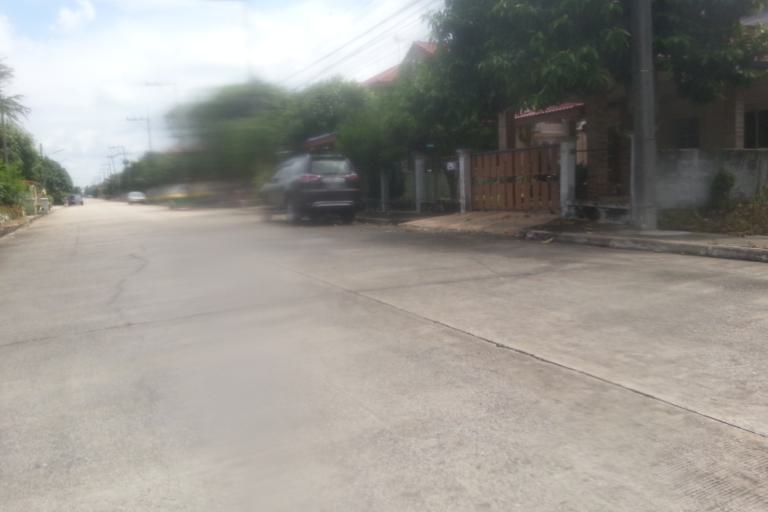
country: TH
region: Pathum Thani
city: Nong Suea
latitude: 14.0588
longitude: 100.8603
